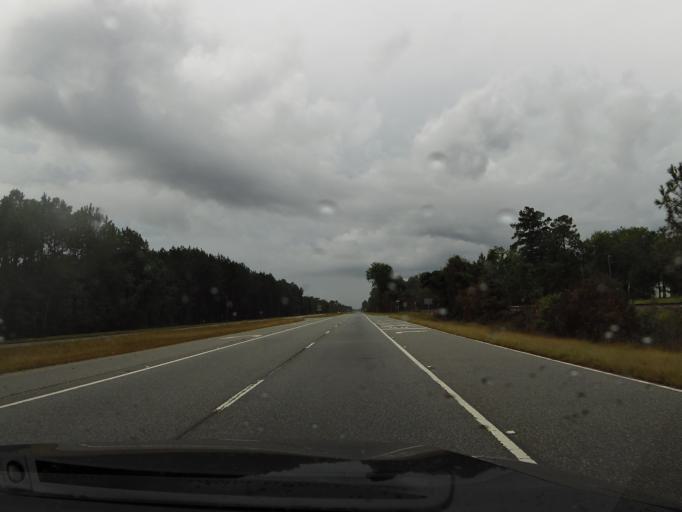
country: US
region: Georgia
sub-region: Wayne County
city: Jesup
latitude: 31.5246
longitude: -81.7827
